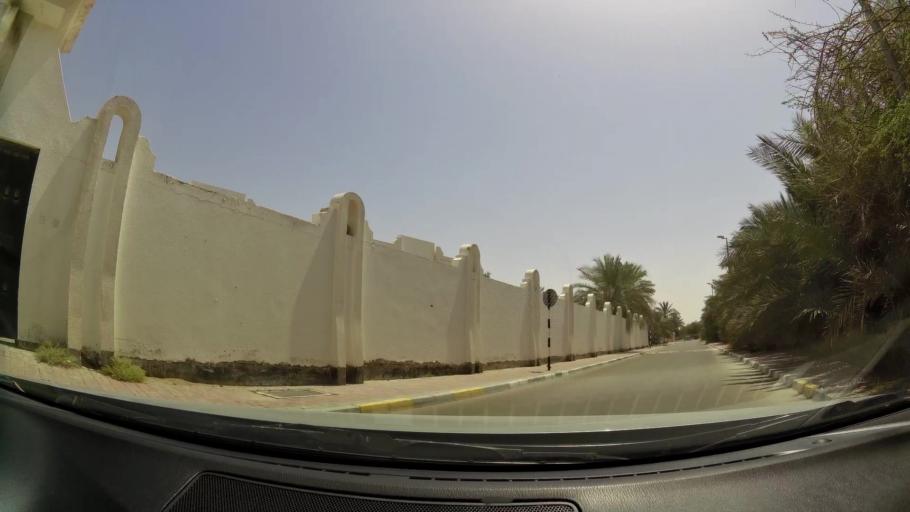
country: OM
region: Al Buraimi
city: Al Buraymi
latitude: 24.2788
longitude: 55.7807
